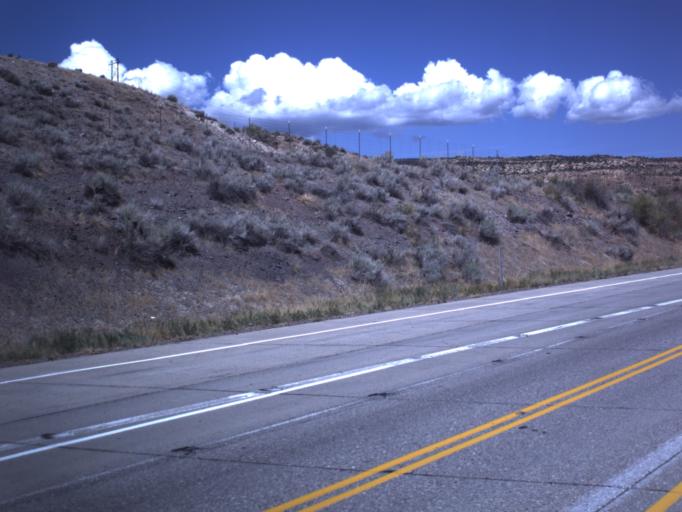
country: US
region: Utah
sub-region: Sevier County
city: Richfield
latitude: 38.7569
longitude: -112.1054
